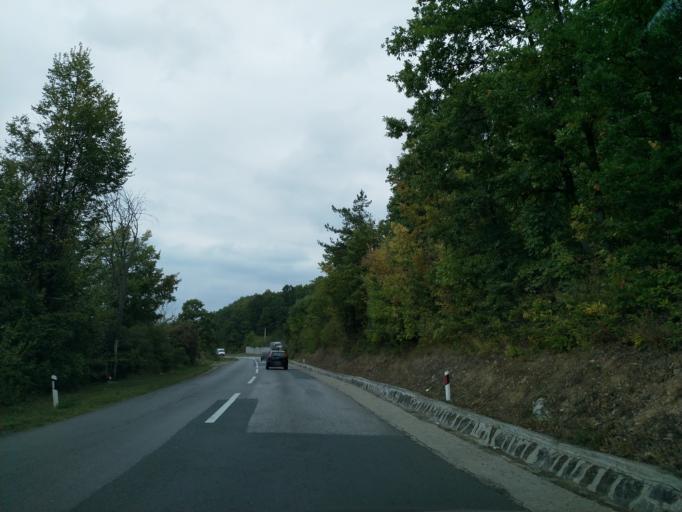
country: RS
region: Central Serbia
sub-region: Sumadijski Okrug
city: Topola
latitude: 44.2331
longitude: 20.7124
